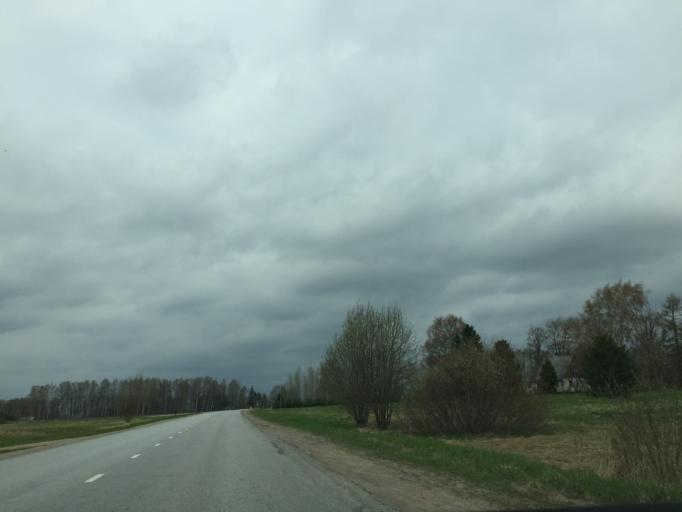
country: EE
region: Tartu
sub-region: Noo vald
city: Noo
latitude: 58.2768
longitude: 26.5305
